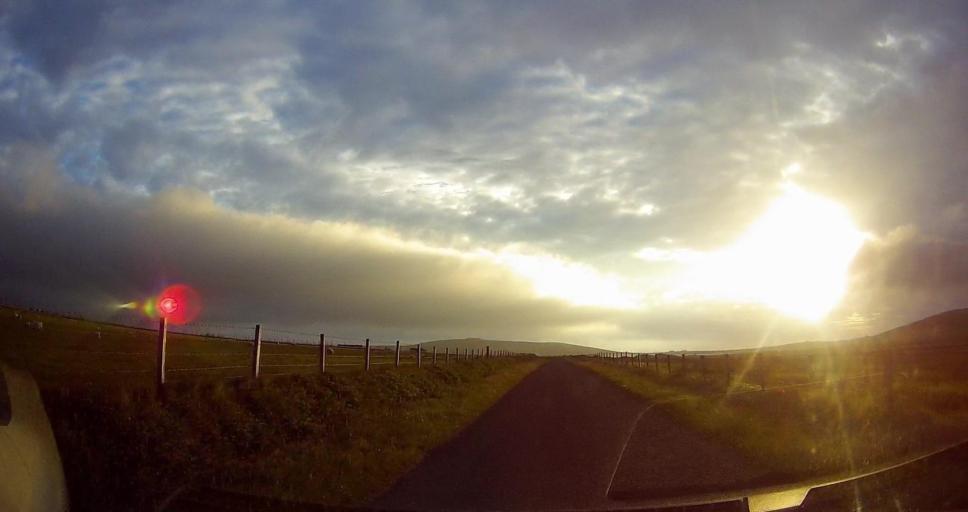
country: GB
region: Scotland
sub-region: Orkney Islands
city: Stromness
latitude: 59.1070
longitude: -3.2380
